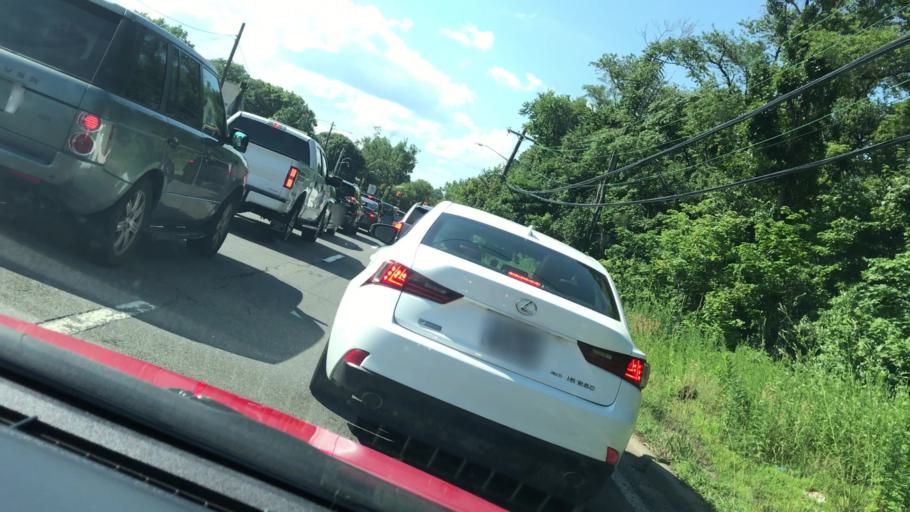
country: US
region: New York
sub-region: Nassau County
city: Lynbrook
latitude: 40.6609
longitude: -73.6575
